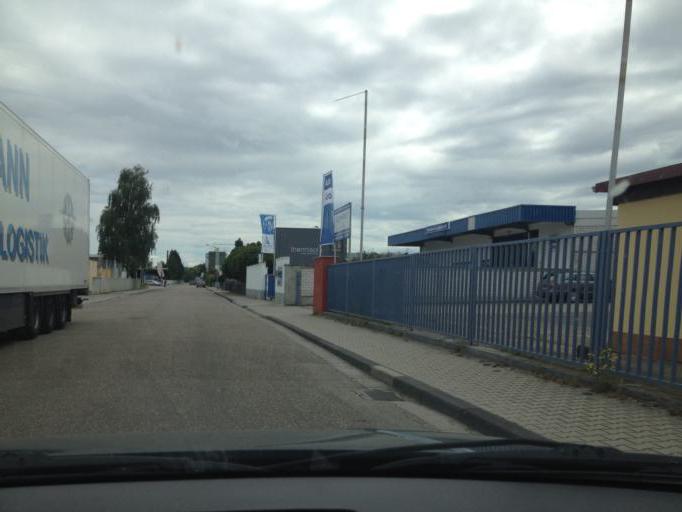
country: DE
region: Rheinland-Pfalz
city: Frankenthal
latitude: 49.5496
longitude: 8.3477
